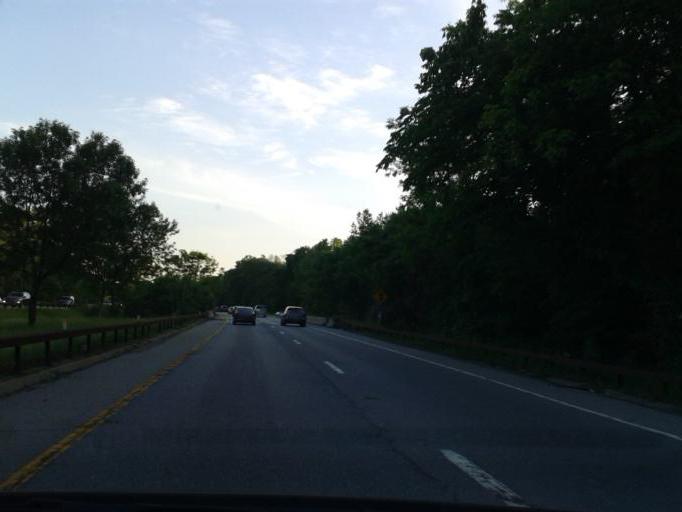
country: US
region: New York
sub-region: Westchester County
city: Harrison
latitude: 40.9997
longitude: -73.7262
